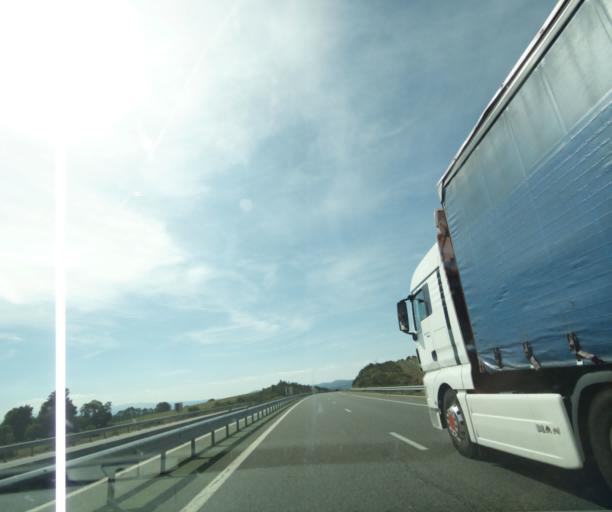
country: FR
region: Auvergne
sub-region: Departement du Puy-de-Dome
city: Saint-Ours
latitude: 45.8731
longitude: 2.9037
